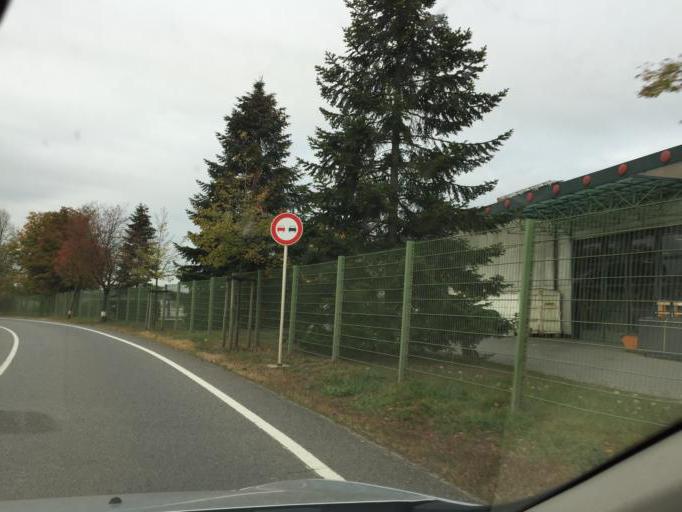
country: LU
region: Luxembourg
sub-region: Canton de Luxembourg
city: Olm
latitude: 49.6647
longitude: 6.0140
